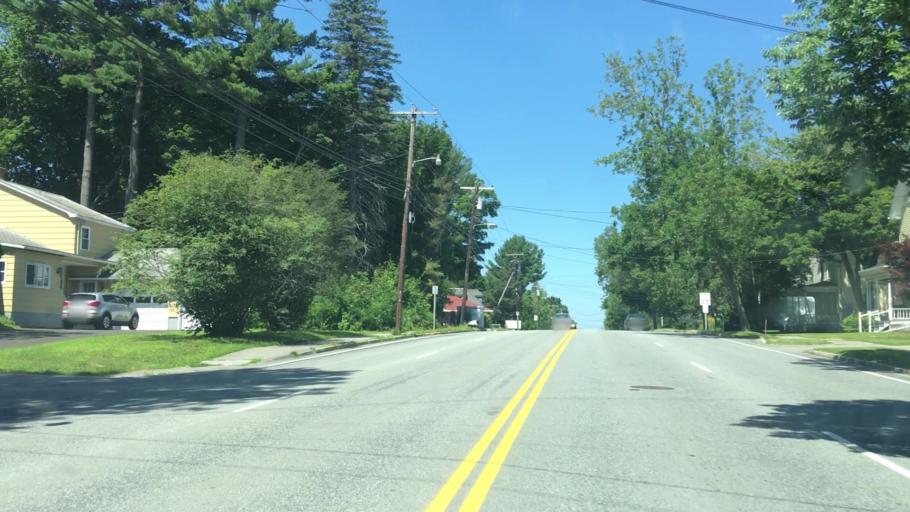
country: US
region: Maine
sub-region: Penobscot County
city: Bangor
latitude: 44.8103
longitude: -68.7962
